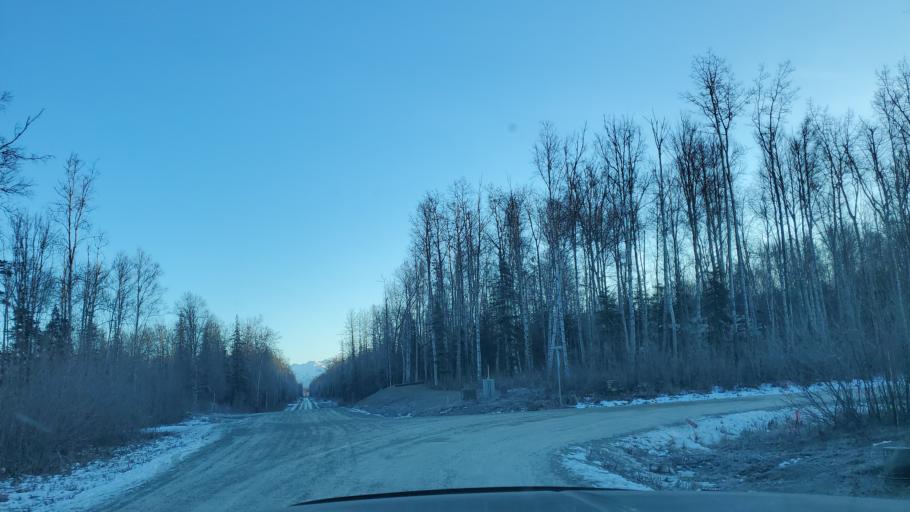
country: US
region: Alaska
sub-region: Matanuska-Susitna Borough
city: Lakes
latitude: 61.6554
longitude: -149.3327
